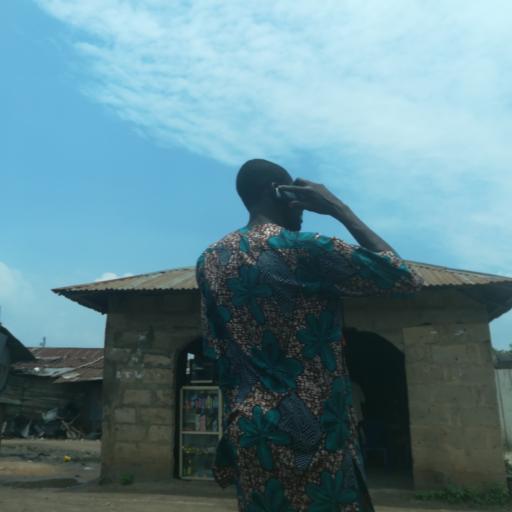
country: NG
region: Lagos
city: Ejirin
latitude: 6.6561
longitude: 3.7949
